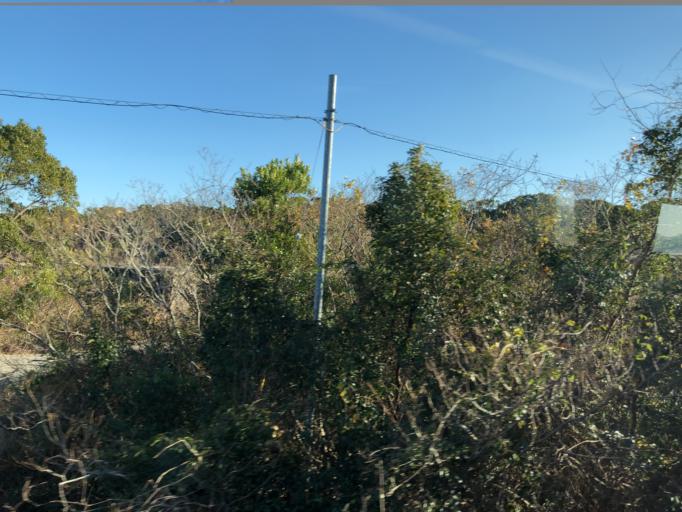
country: JP
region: Kochi
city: Nakamura
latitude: 33.0308
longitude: 133.0168
